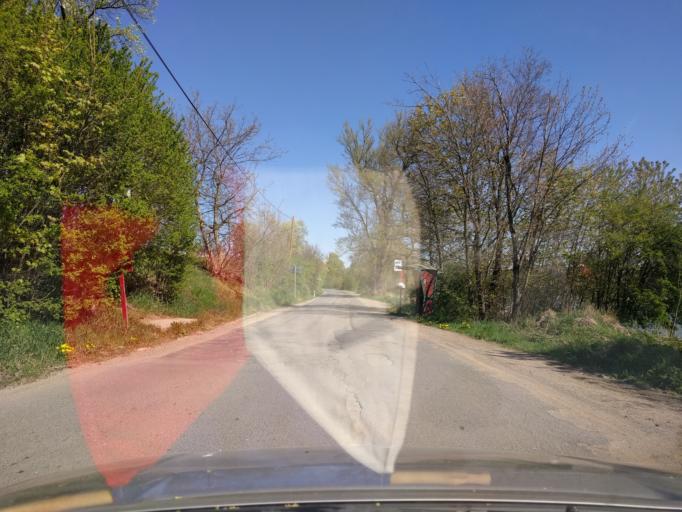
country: CZ
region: Central Bohemia
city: Cesky Brod
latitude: 50.0577
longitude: 14.8468
